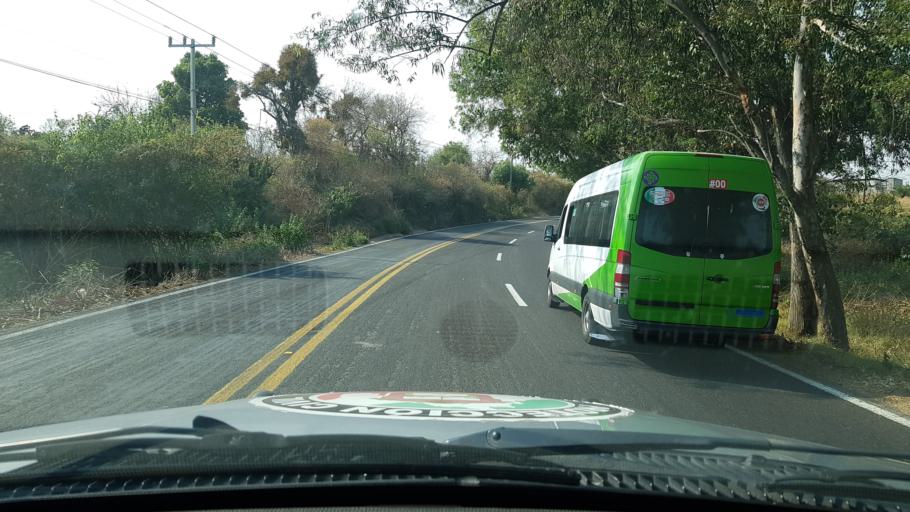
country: MX
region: Mexico
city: Tepetlixpa
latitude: 19.0091
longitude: -98.8237
